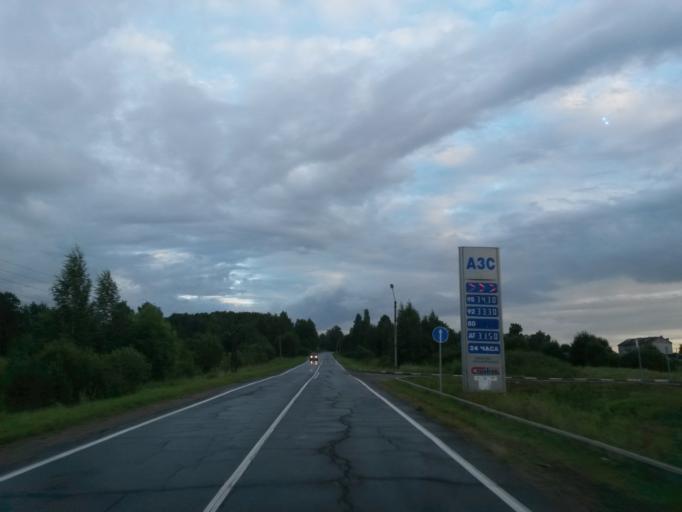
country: RU
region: Jaroslavl
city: Tutayev
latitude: 57.9006
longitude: 39.5250
